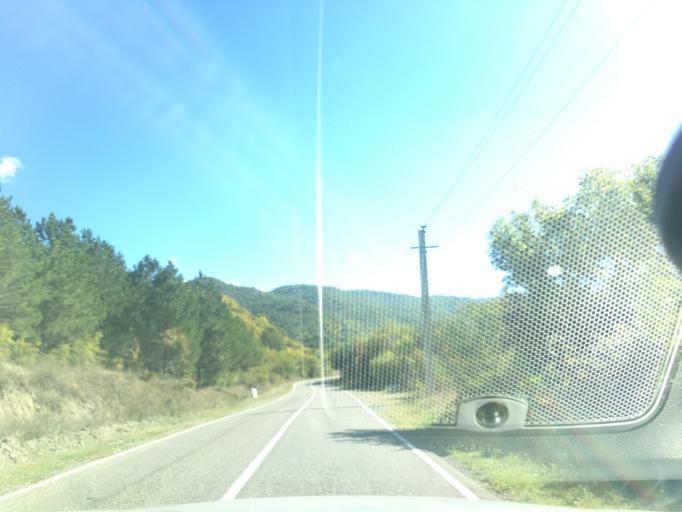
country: GE
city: Zahesi
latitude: 41.8425
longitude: 44.8795
